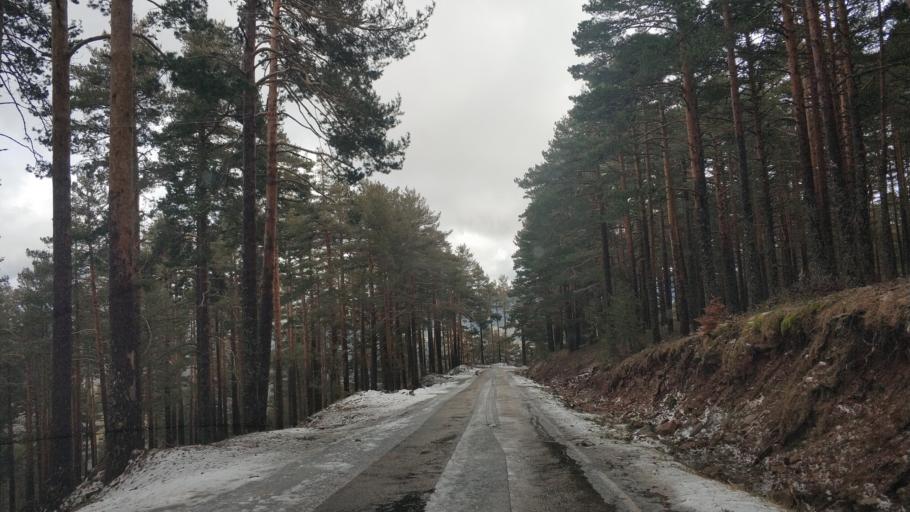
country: ES
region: Castille and Leon
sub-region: Provincia de Burgos
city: Neila
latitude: 42.0469
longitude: -3.0285
